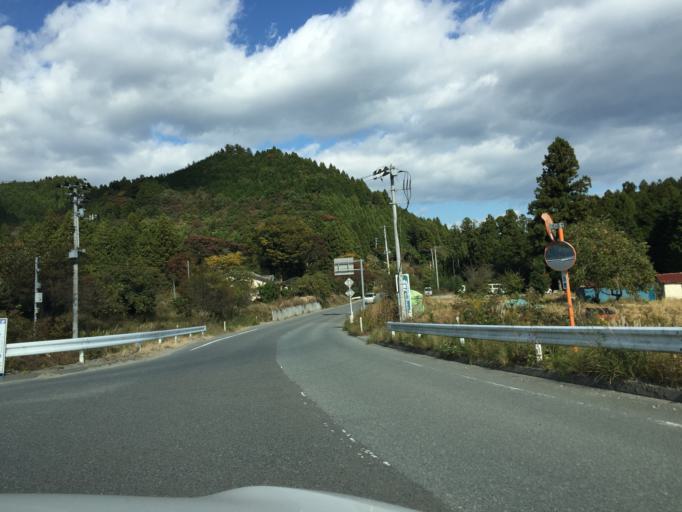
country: JP
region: Fukushima
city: Namie
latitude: 37.3663
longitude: 140.9518
